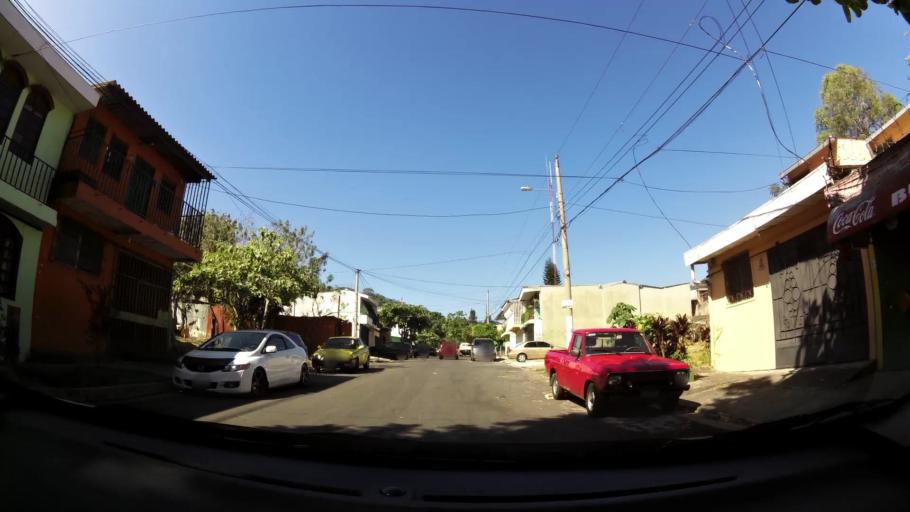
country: SV
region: La Libertad
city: Santa Tecla
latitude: 13.6677
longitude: -89.2866
